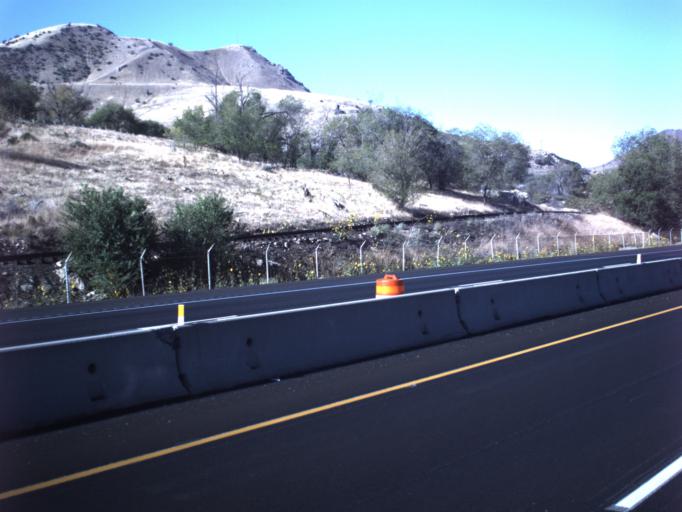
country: US
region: Utah
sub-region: Salt Lake County
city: Magna
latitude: 40.7174
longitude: -112.1358
